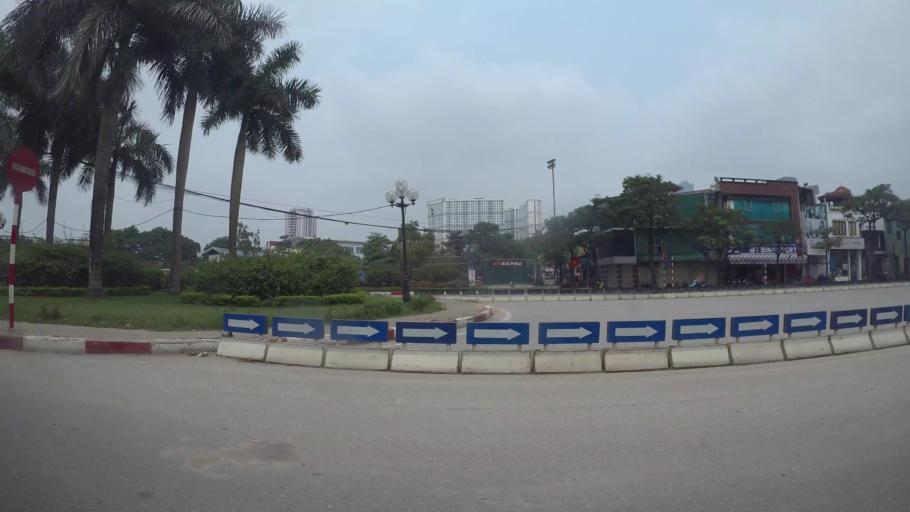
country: VN
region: Ha Noi
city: Cau Dien
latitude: 21.0141
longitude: 105.7694
